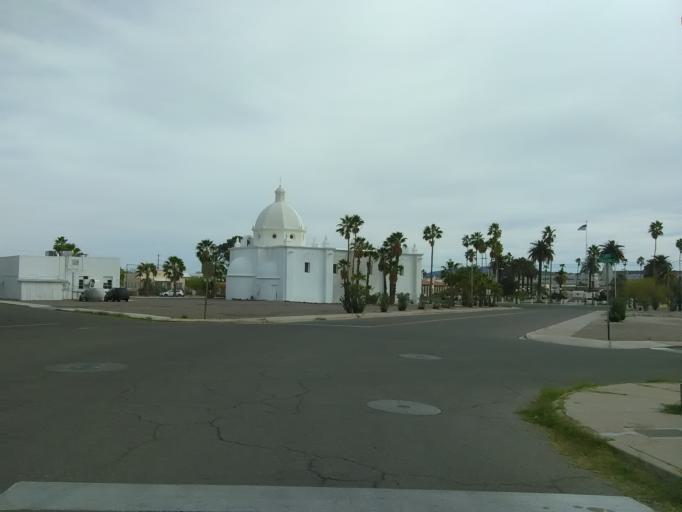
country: US
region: Arizona
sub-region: Pima County
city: Ajo
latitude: 32.3721
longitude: -112.8640
